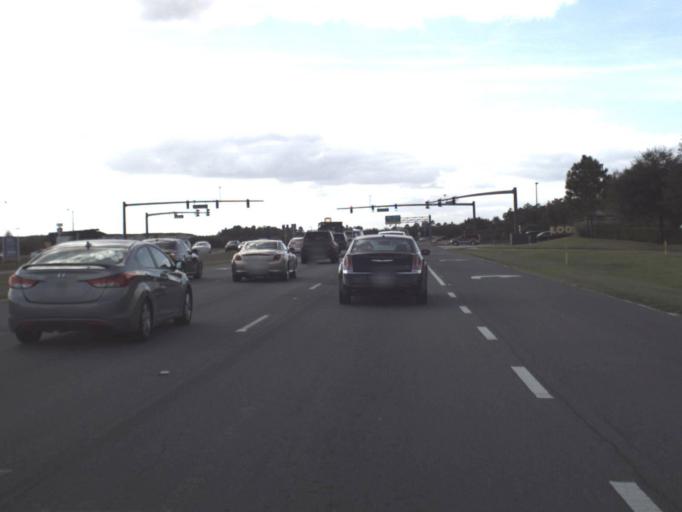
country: US
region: Florida
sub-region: Orange County
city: Hunters Creek
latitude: 28.3421
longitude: -81.4296
